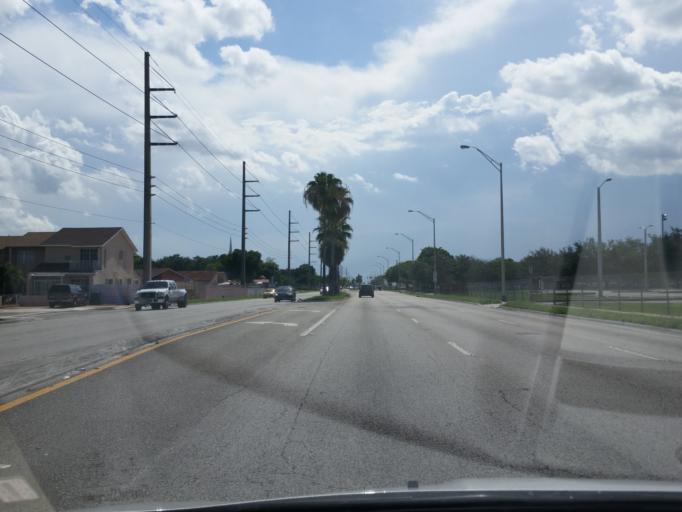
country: US
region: Florida
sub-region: Miami-Dade County
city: Fountainebleau
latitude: 25.7690
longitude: -80.3539
